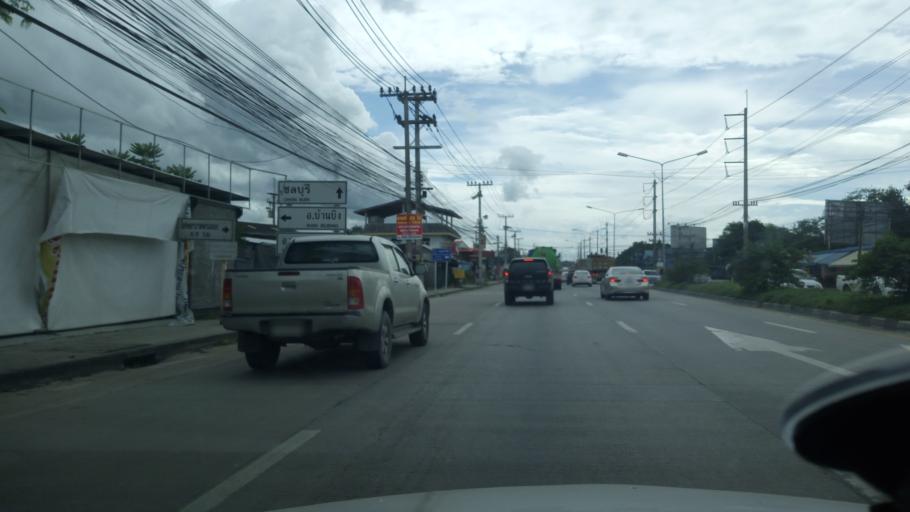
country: TH
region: Chon Buri
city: Phan Thong
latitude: 13.4251
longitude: 101.1117
